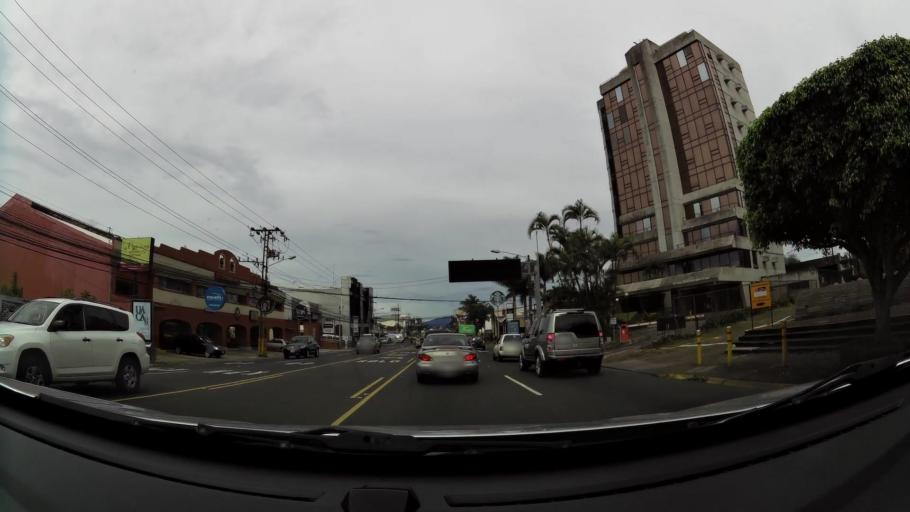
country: CR
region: San Jose
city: San Pedro
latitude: 9.9253
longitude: -84.0396
